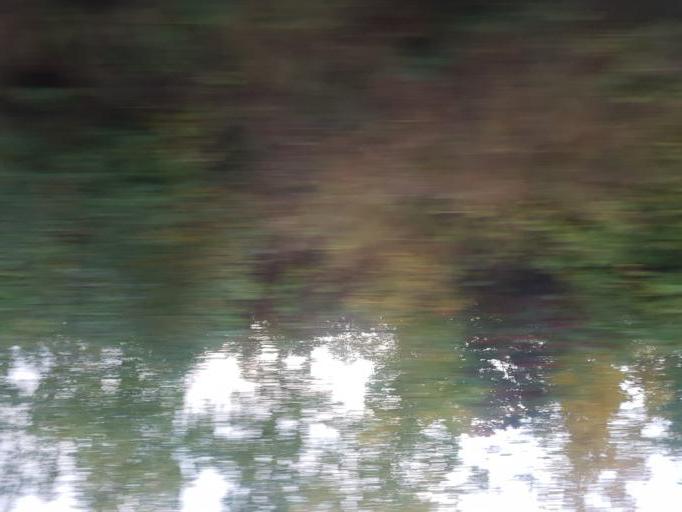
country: NO
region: Sor-Trondelag
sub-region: Trondheim
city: Trondheim
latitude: 63.4107
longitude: 10.3910
